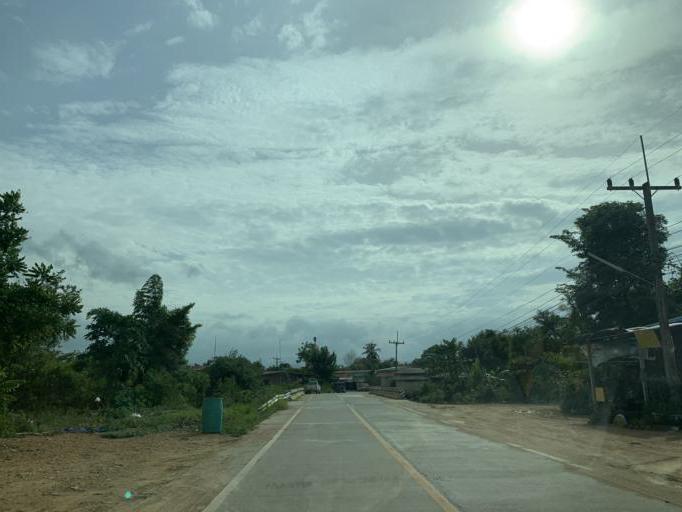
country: TH
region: Nakhon Sawan
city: Mae Wong
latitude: 15.8418
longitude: 99.4187
